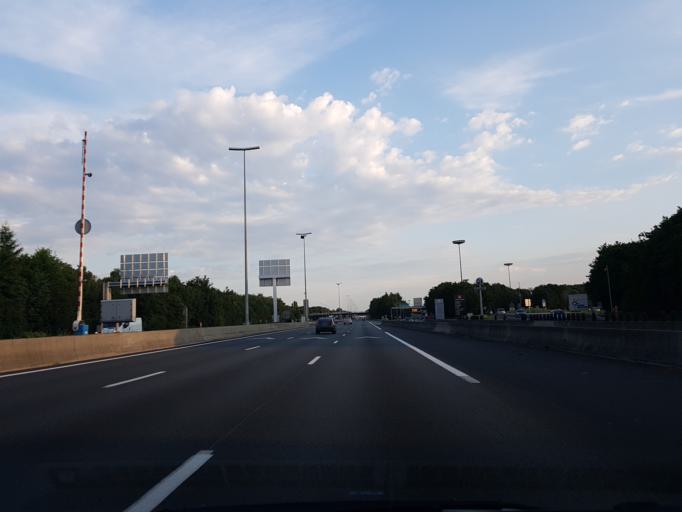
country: FR
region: Ile-de-France
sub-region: Departement du Val-d'Oise
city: Roissy-en-France
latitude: 49.0158
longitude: 2.5313
